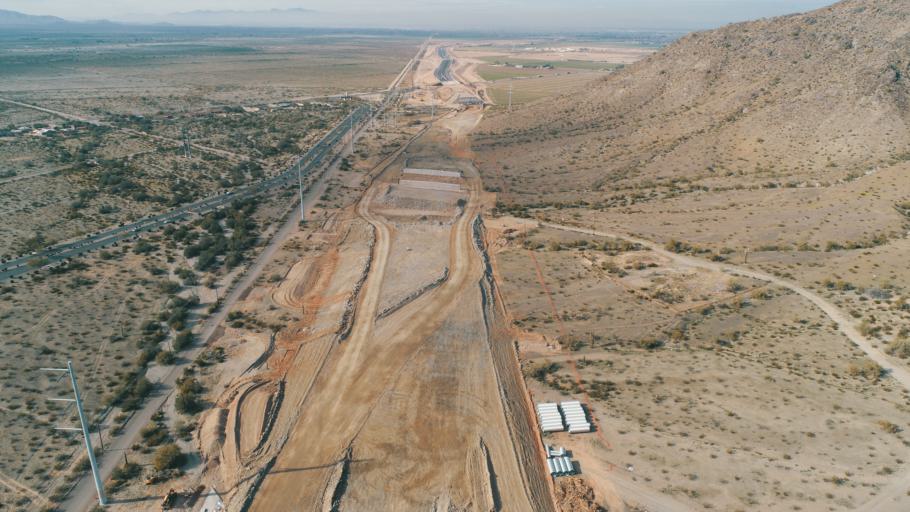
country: US
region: Arizona
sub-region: Maricopa County
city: Laveen
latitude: 33.3163
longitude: -112.1584
